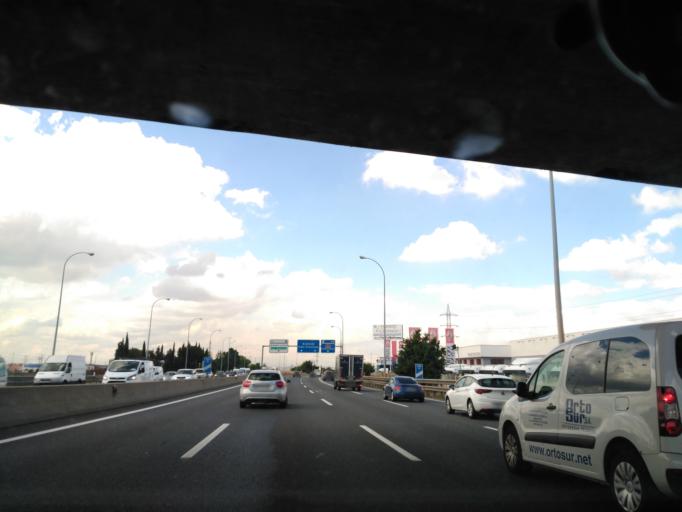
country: ES
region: Madrid
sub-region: Provincia de Madrid
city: Villaverde
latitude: 40.3191
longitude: -3.6921
